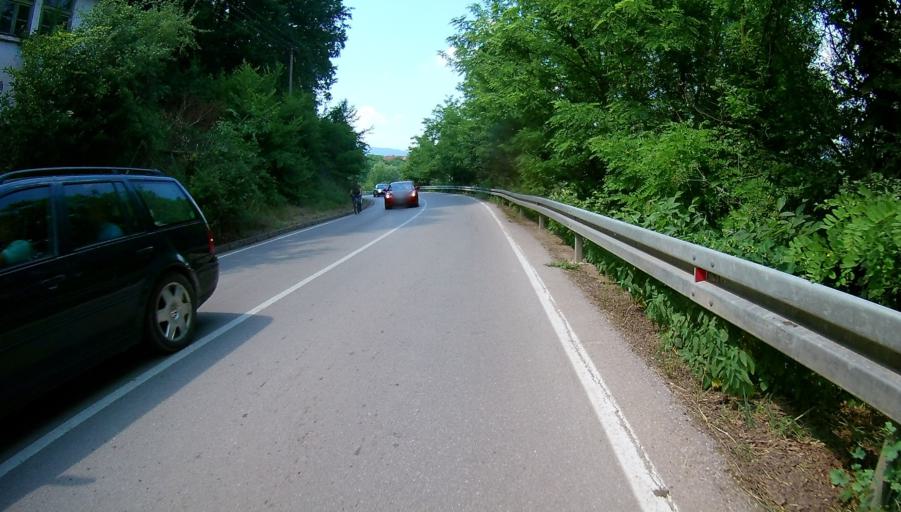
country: RS
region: Central Serbia
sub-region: Nisavski Okrug
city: Gadzin Han
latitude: 43.2031
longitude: 22.0212
